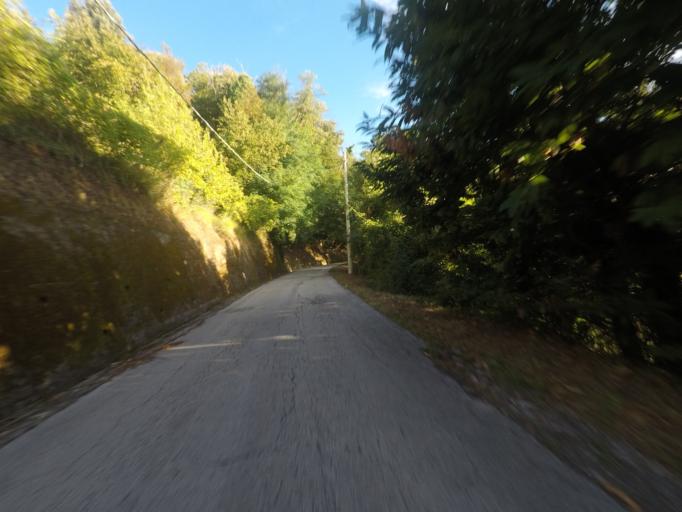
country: IT
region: Tuscany
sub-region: Provincia di Lucca
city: Stiava
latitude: 43.9180
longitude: 10.3698
